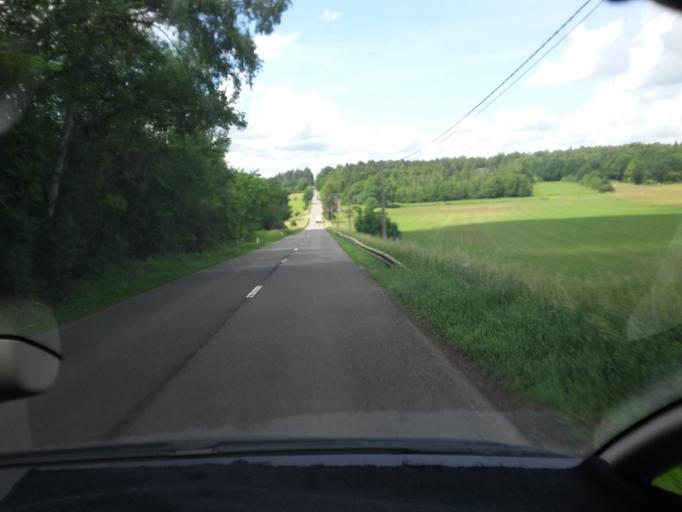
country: BE
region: Wallonia
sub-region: Province de Namur
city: Rochefort
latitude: 50.1282
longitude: 5.2394
